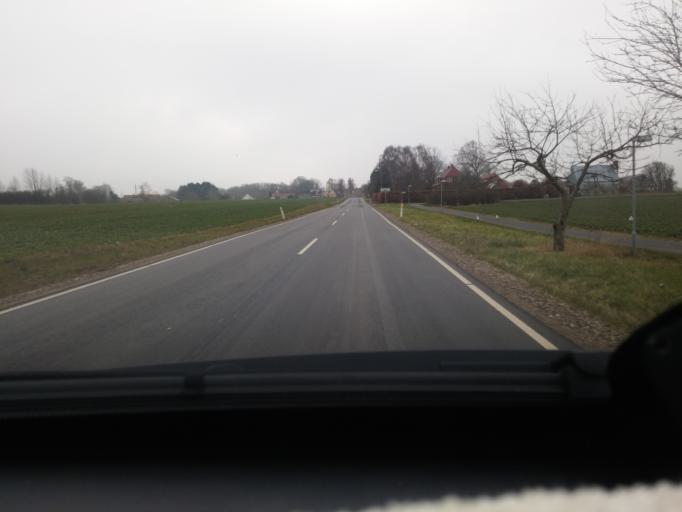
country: DK
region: South Denmark
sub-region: Nyborg Kommune
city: Ullerslev
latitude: 55.3720
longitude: 10.7273
